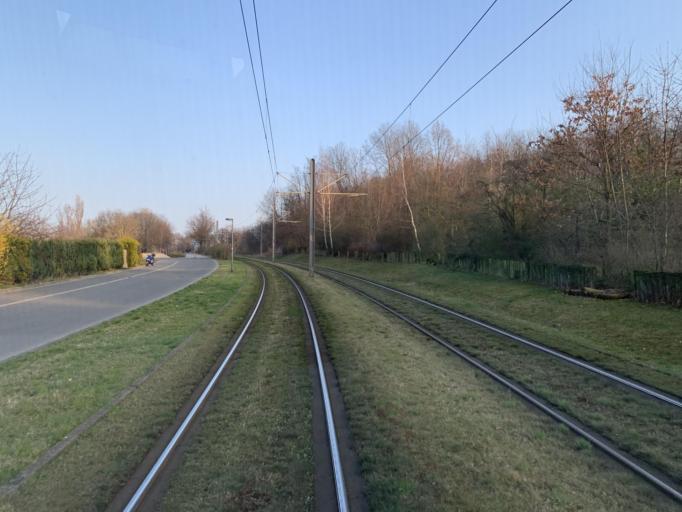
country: DE
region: Saxony
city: Bannewitz
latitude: 51.0239
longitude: 13.7174
